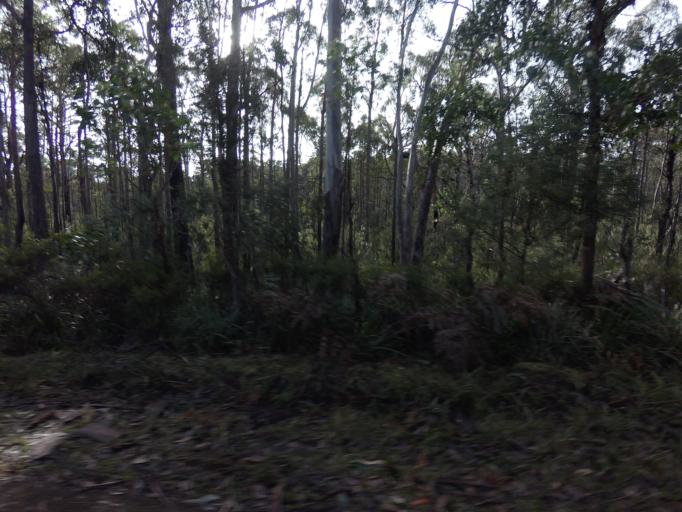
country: AU
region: Tasmania
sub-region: Derwent Valley
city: New Norfolk
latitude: -42.7636
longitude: 146.8971
